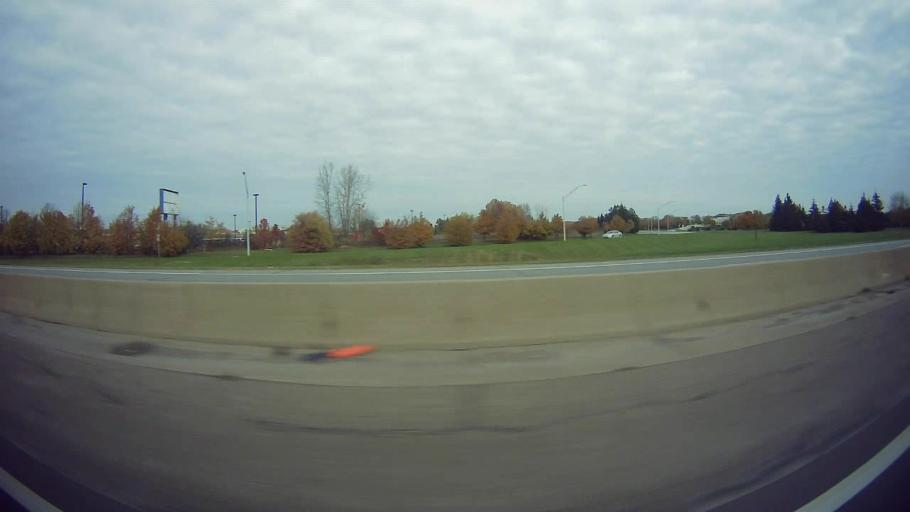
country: US
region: Michigan
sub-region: Wayne County
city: Romulus
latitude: 42.2389
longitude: -83.3435
